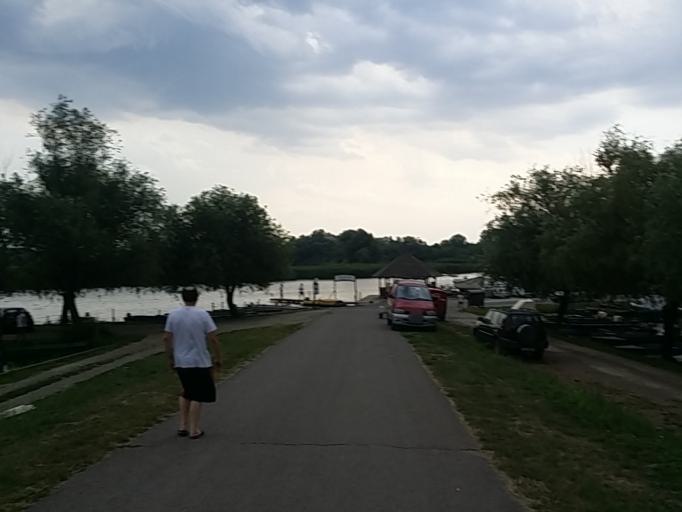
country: HU
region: Heves
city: Poroszlo
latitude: 47.6403
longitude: 20.6535
